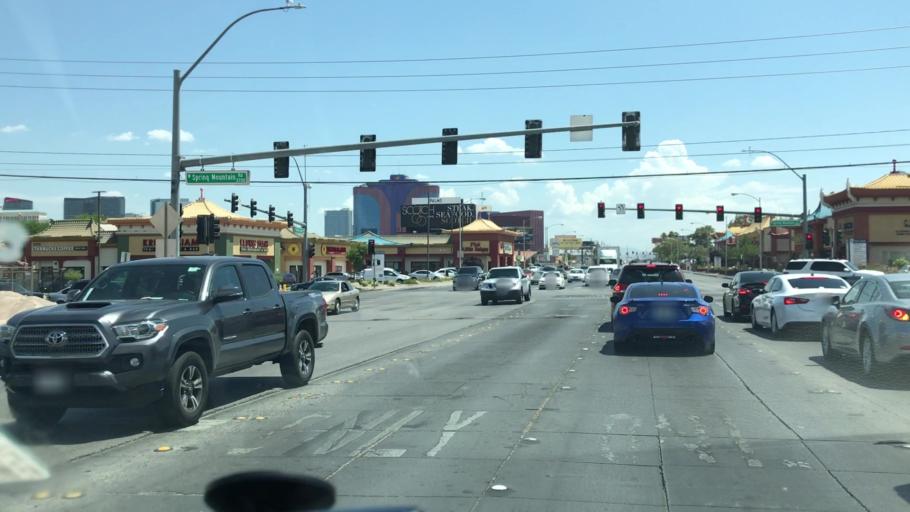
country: US
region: Nevada
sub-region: Clark County
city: Paradise
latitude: 36.1270
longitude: -115.1902
